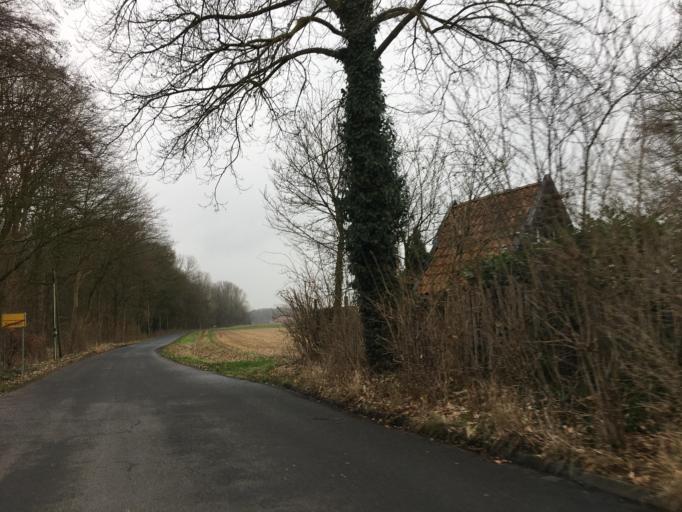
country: DE
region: North Rhine-Westphalia
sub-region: Regierungsbezirk Munster
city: Senden
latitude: 51.8602
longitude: 7.4700
